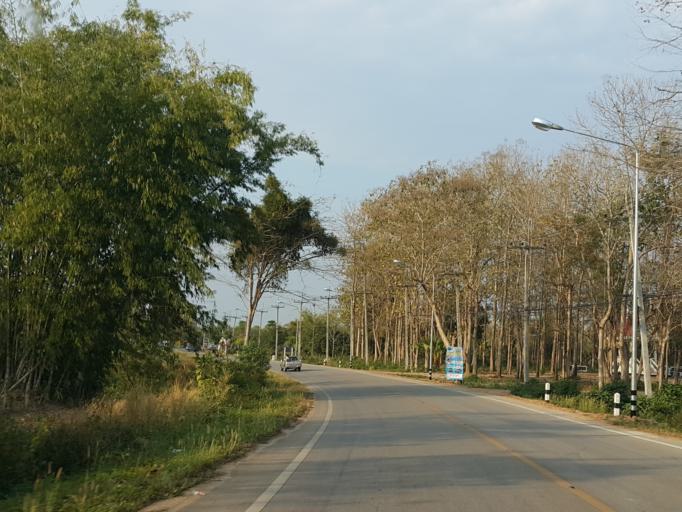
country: TH
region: Lampang
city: Chae Hom
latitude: 18.5259
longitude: 99.4776
